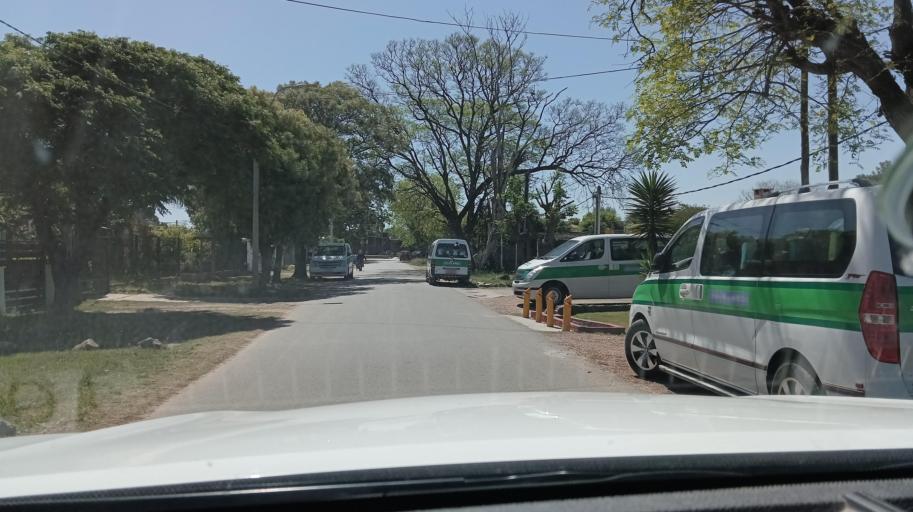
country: UY
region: Canelones
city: Paso de Carrasco
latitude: -34.8532
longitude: -56.0414
